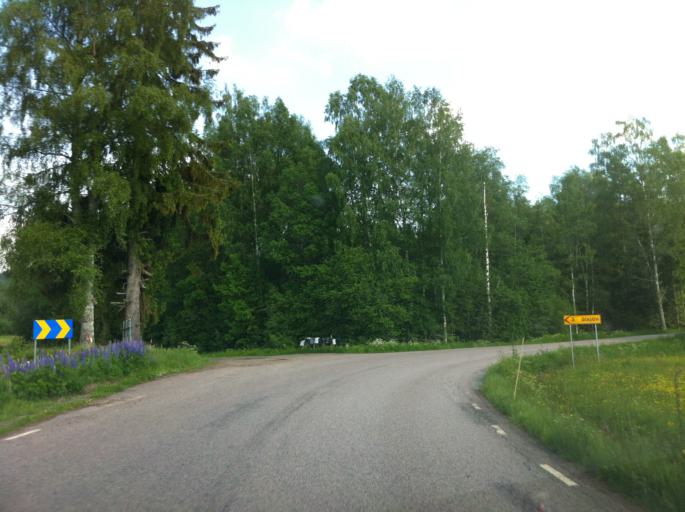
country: SE
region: Vaermland
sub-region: Kils Kommun
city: Kil
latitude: 59.6869
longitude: 13.2659
